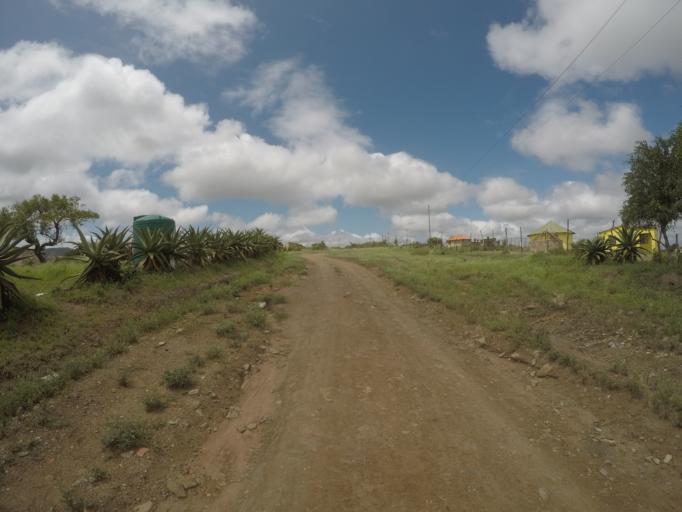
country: ZA
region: KwaZulu-Natal
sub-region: uThungulu District Municipality
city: Empangeni
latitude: -28.5748
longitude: 31.8402
